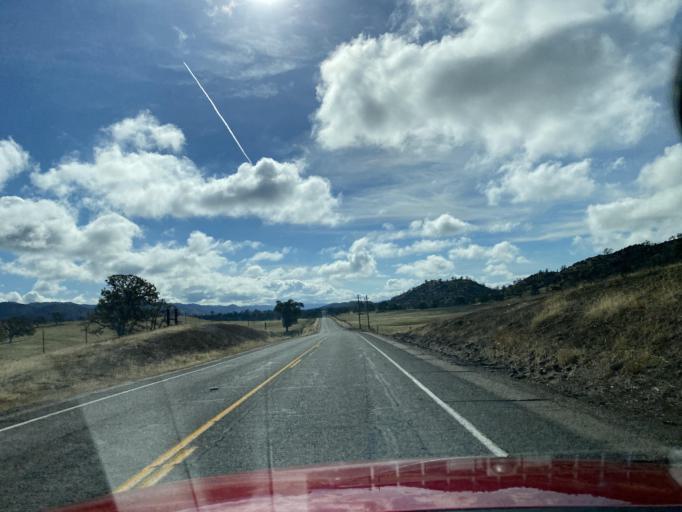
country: US
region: California
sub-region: Glenn County
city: Willows
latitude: 39.5309
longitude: -122.5329
